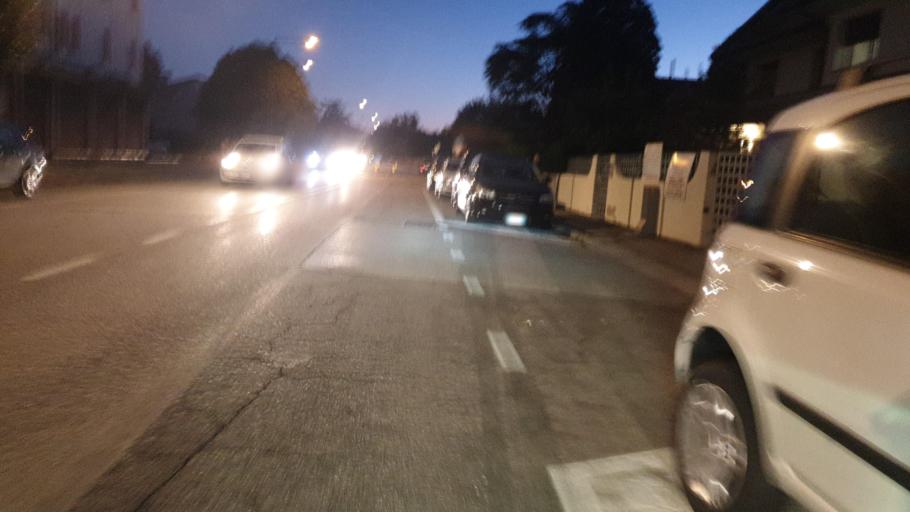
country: IT
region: Veneto
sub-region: Provincia di Padova
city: Oltre Brenta
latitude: 45.4148
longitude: 12.0058
